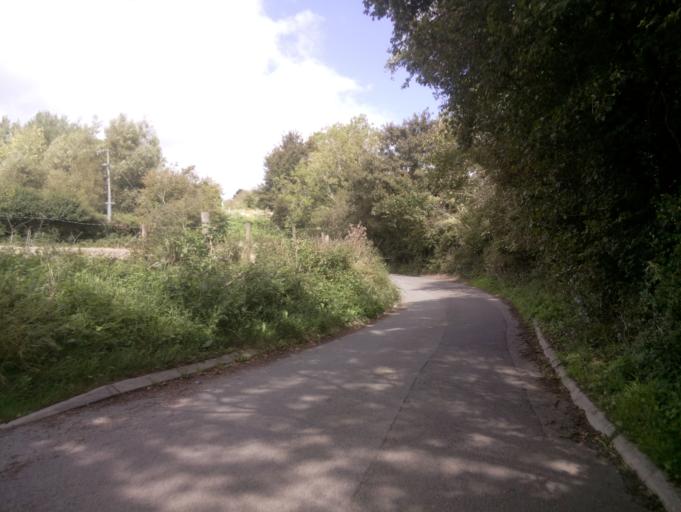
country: GB
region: England
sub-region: Wiltshire
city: Colerne
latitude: 51.4358
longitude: -2.2612
